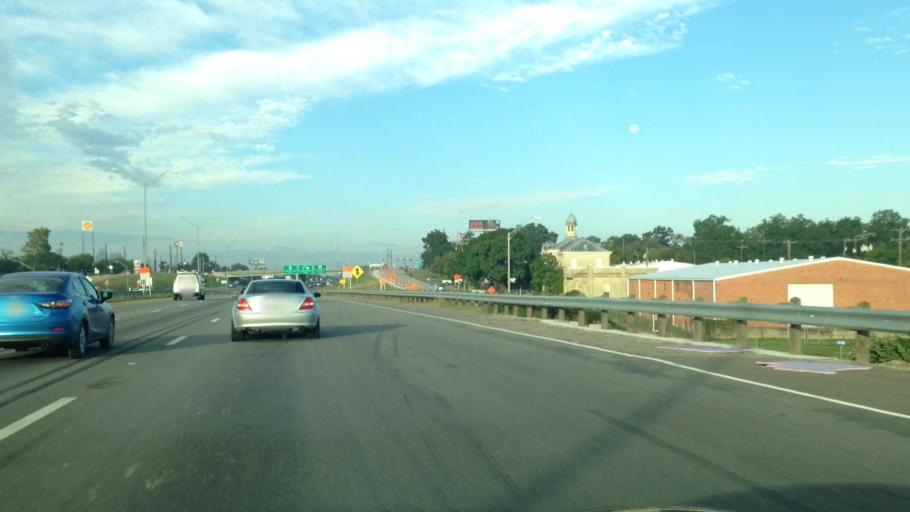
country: US
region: Texas
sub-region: Bexar County
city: Terrell Hills
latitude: 29.4393
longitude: -98.4558
